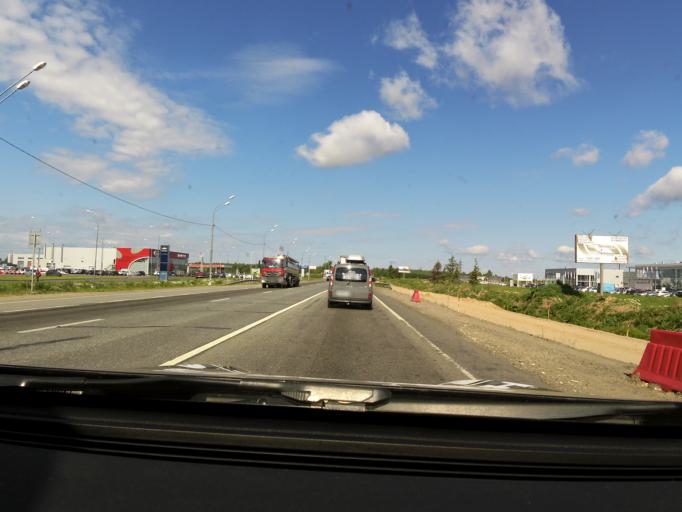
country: RU
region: Tverskaya
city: Tver
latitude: 56.7894
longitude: 35.9091
